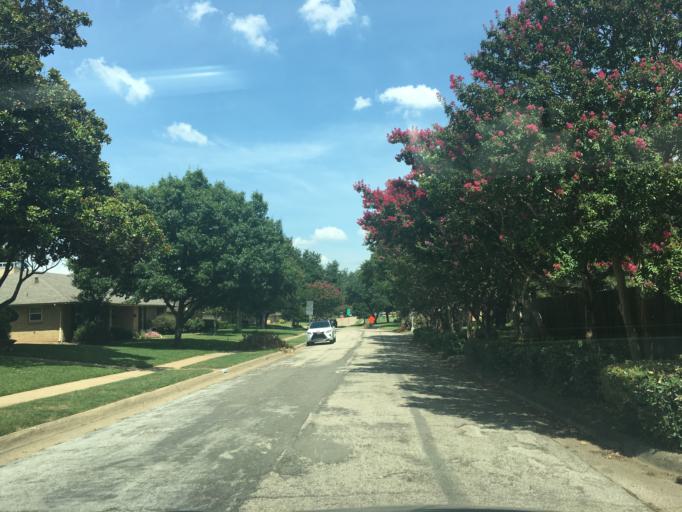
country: US
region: Texas
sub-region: Dallas County
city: Addison
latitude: 32.9177
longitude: -96.8487
